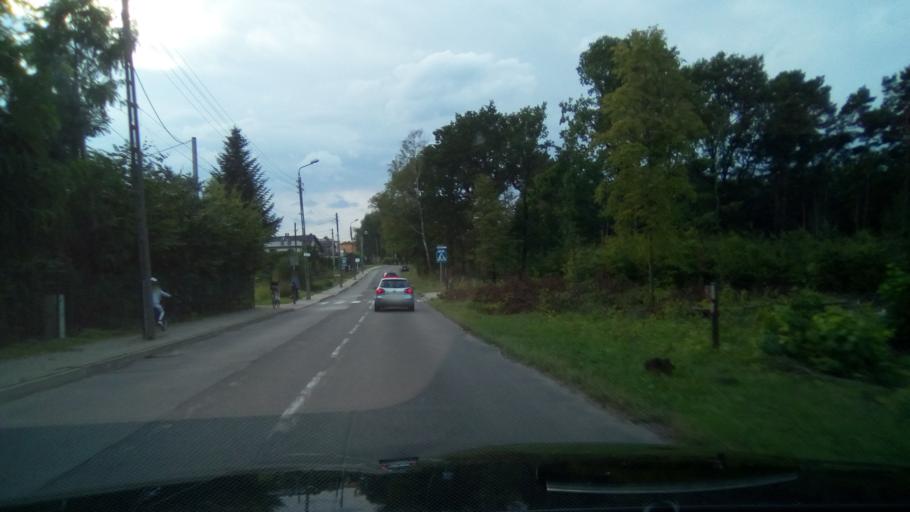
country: PL
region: Silesian Voivodeship
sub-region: Myslowice
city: Myslowice
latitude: 50.2095
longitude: 19.1415
